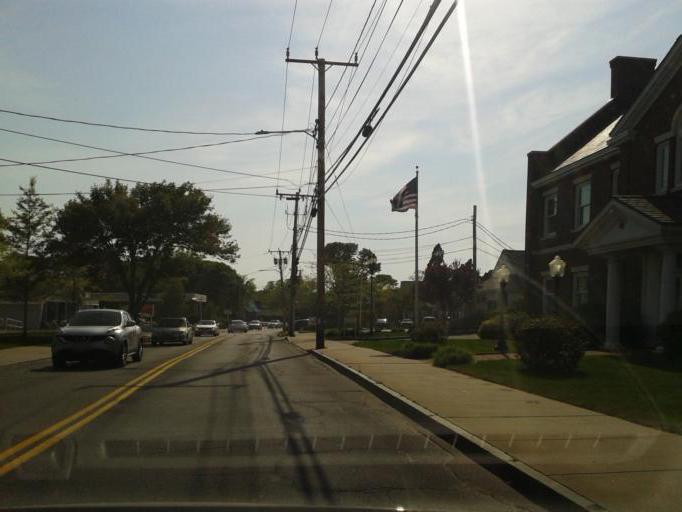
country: US
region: Massachusetts
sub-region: Barnstable County
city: Falmouth
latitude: 41.5527
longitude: -70.6048
